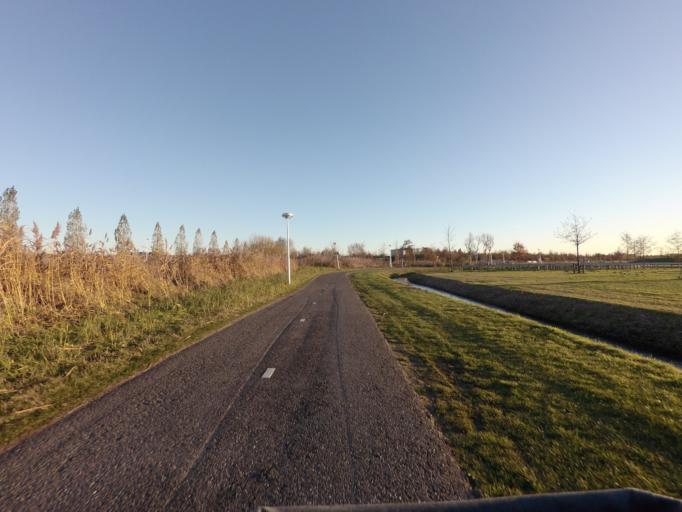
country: NL
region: Utrecht
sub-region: Stichtse Vecht
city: Spechtenkamp
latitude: 52.1163
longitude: 5.0287
